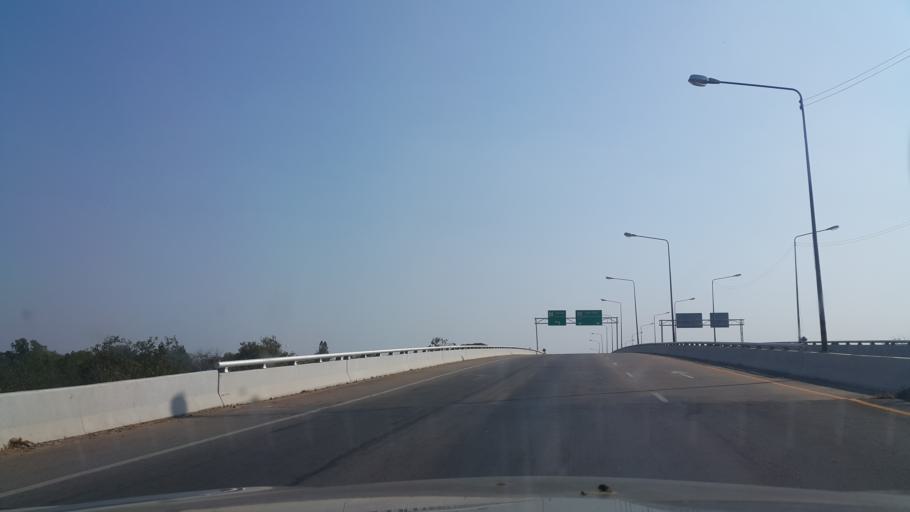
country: TH
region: Khon Kaen
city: Khon Kaen
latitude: 16.4389
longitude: 102.9180
